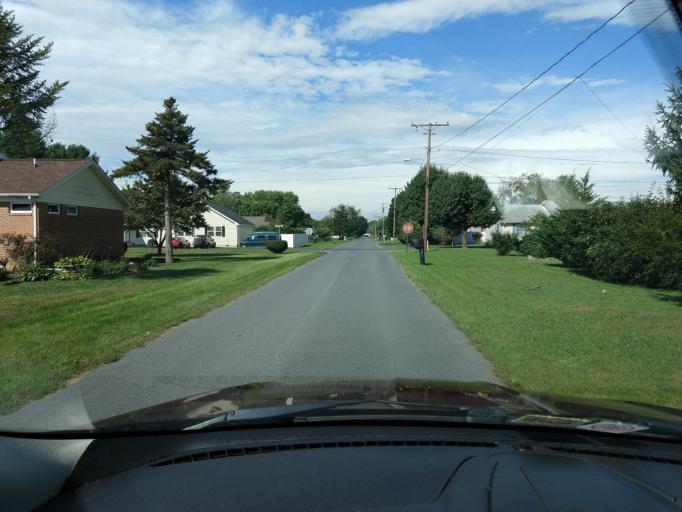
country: US
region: Virginia
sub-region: Rockingham County
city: Grottoes
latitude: 38.2683
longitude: -78.8286
